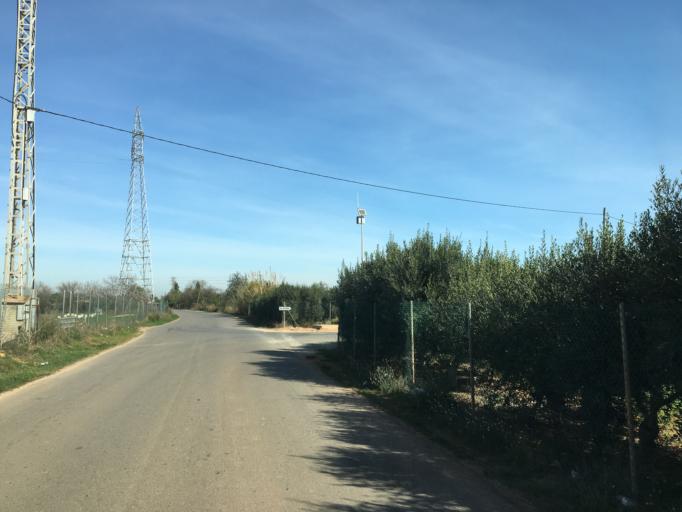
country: ES
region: Murcia
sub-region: Murcia
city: Cartagena
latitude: 37.6501
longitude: -1.0252
